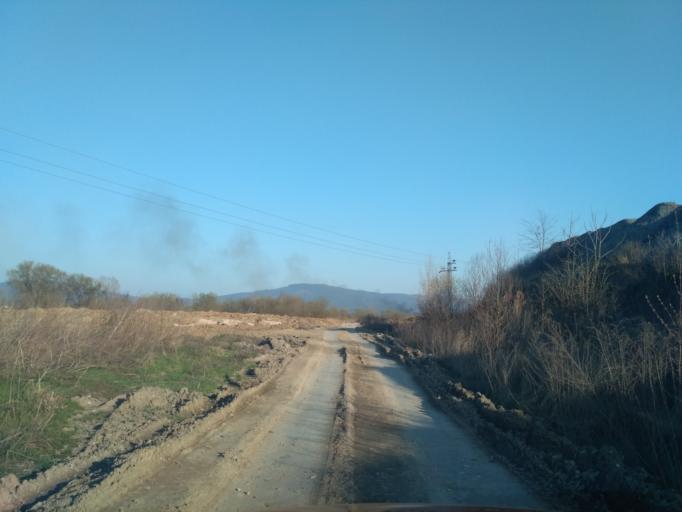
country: SK
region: Kosicky
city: Kosice
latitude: 48.6697
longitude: 21.3008
